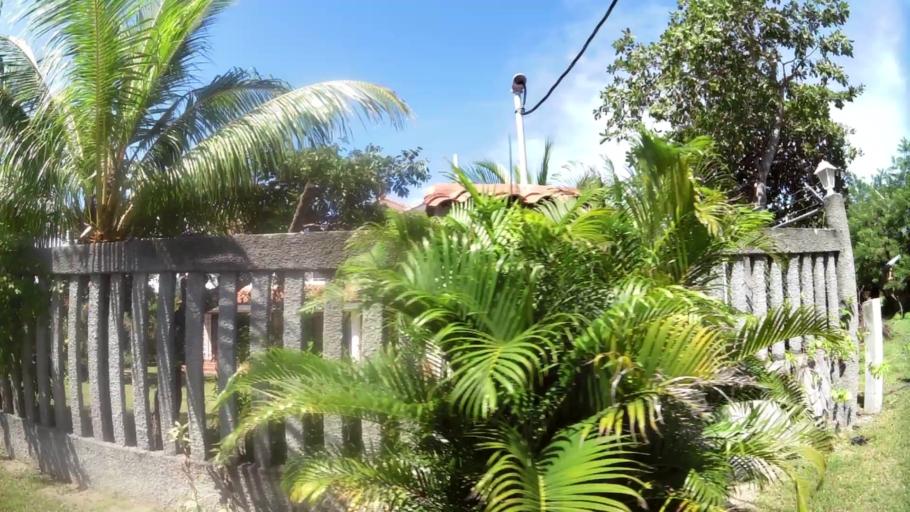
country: PA
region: Panama
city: Nueva Gorgona
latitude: 8.5558
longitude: -79.8582
